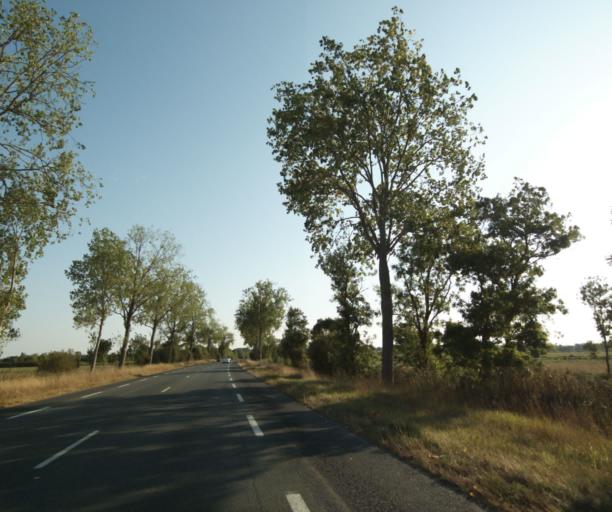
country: FR
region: Poitou-Charentes
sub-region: Departement de la Charente-Maritime
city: Saint-Hippolyte
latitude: 45.9266
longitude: -0.8789
